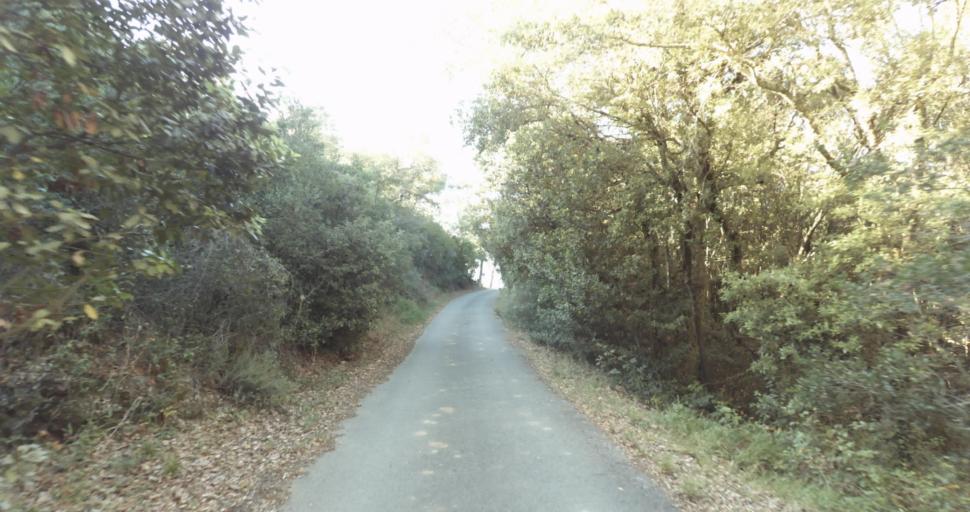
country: FR
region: Provence-Alpes-Cote d'Azur
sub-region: Departement du Var
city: Gassin
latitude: 43.2324
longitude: 6.5952
